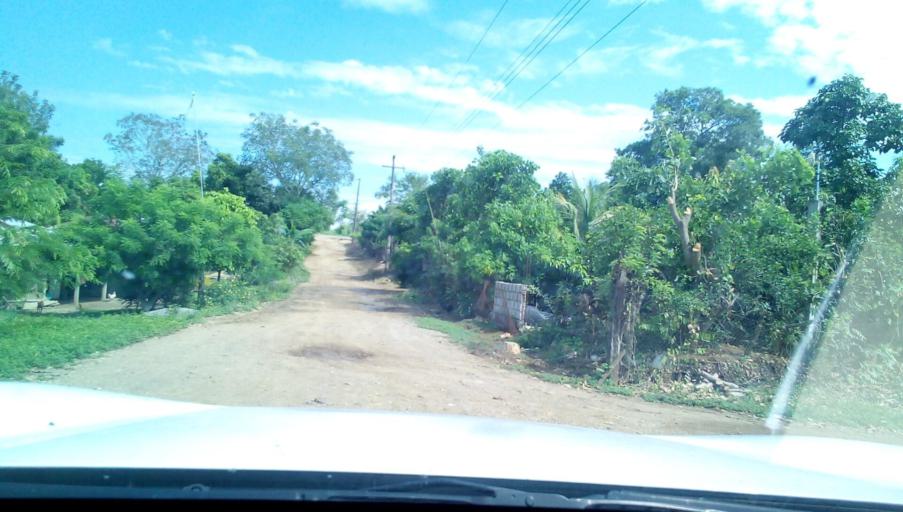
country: MX
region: Veracruz
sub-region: Alamo Temapache
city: Vegas de la Soledad y Soledad Dos
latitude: 20.8966
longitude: -97.9451
